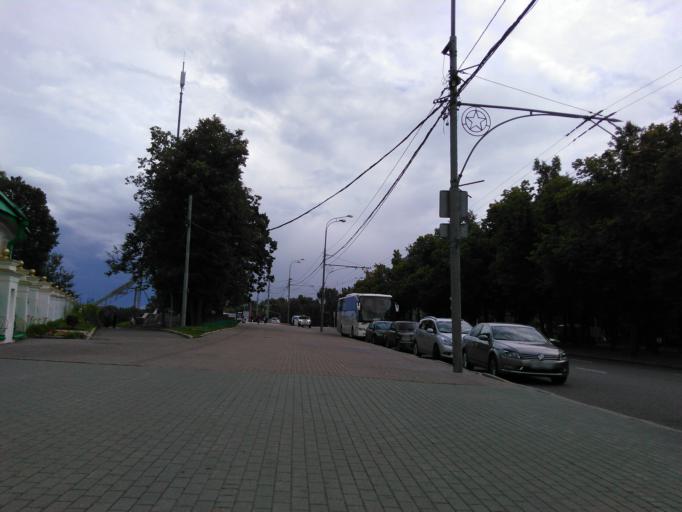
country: RU
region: Moscow
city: Vorob'yovo
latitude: 55.7107
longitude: 37.5399
